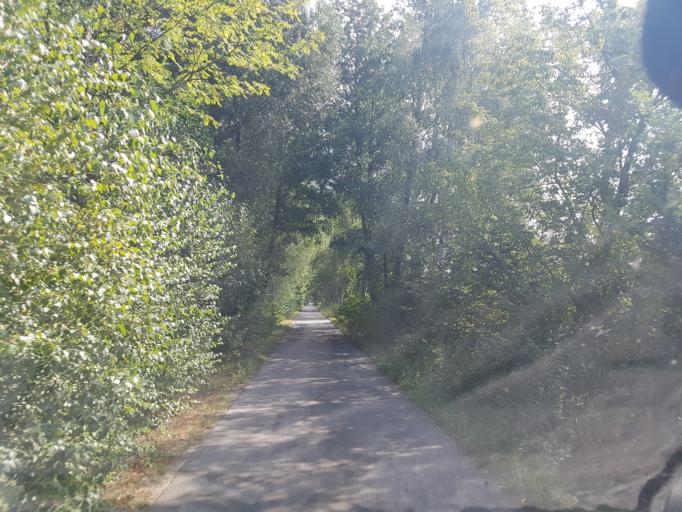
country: DE
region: Brandenburg
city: Finsterwalde
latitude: 51.6631
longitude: 13.7455
